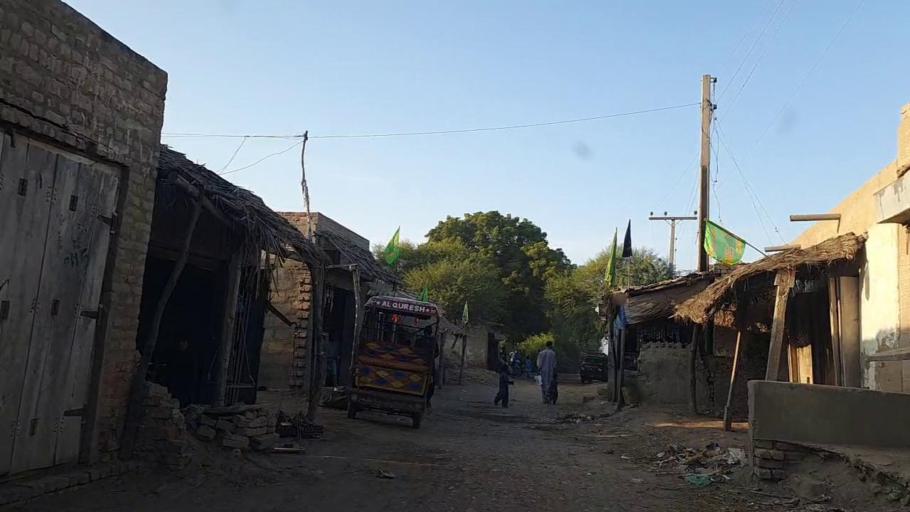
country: PK
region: Sindh
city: Mirpur Batoro
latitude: 24.7059
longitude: 68.2161
